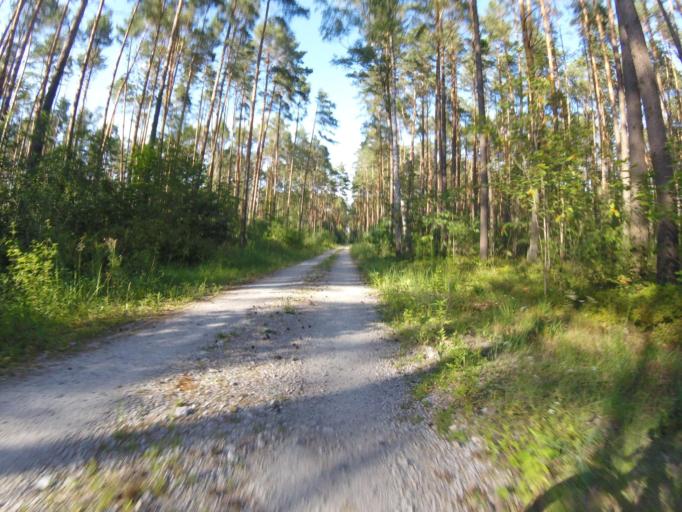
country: DE
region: Brandenburg
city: Erkner
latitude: 52.3319
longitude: 13.7370
